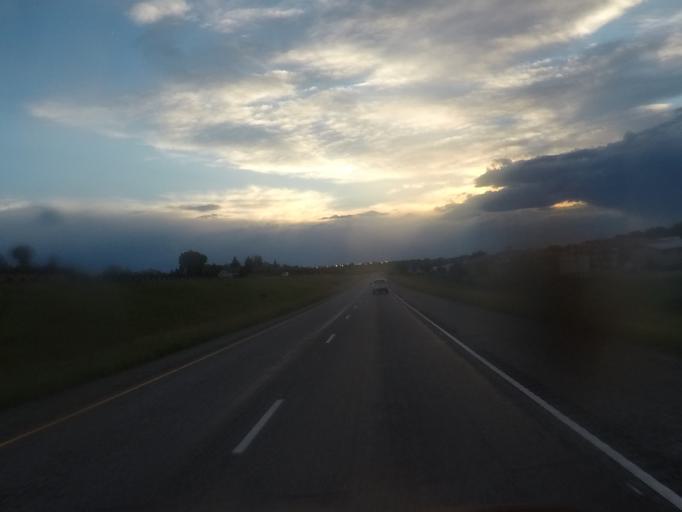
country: US
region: Montana
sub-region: Gallatin County
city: Bozeman
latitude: 45.6695
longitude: -110.9927
